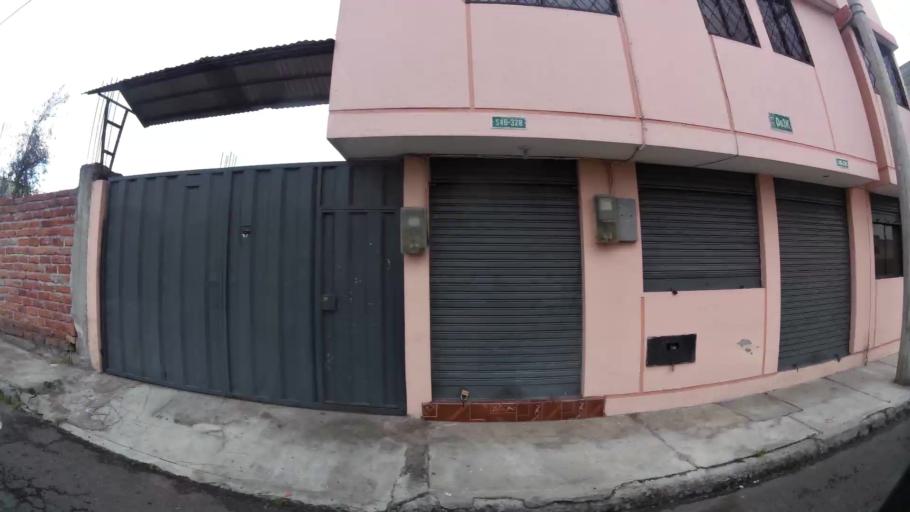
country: EC
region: Pichincha
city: Quito
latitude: -0.3123
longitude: -78.5561
